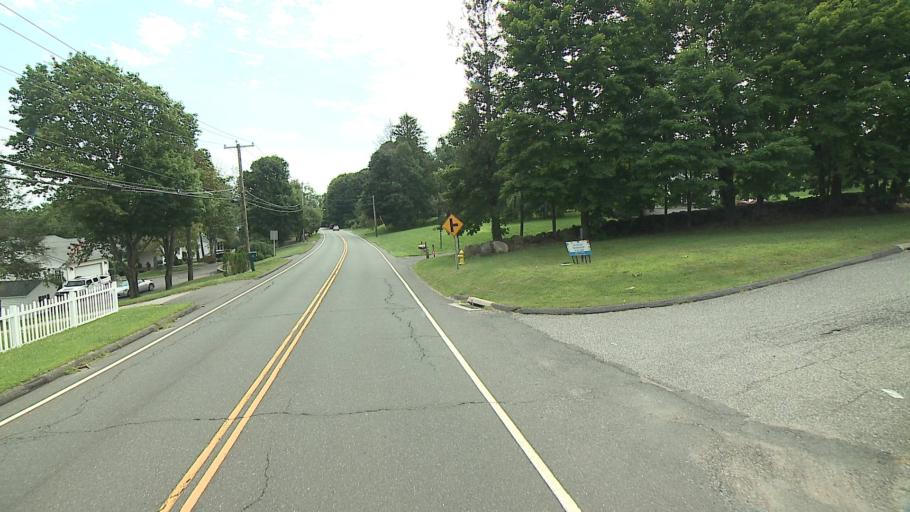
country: US
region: Connecticut
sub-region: Fairfield County
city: Danbury
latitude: 41.4279
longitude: -73.4854
